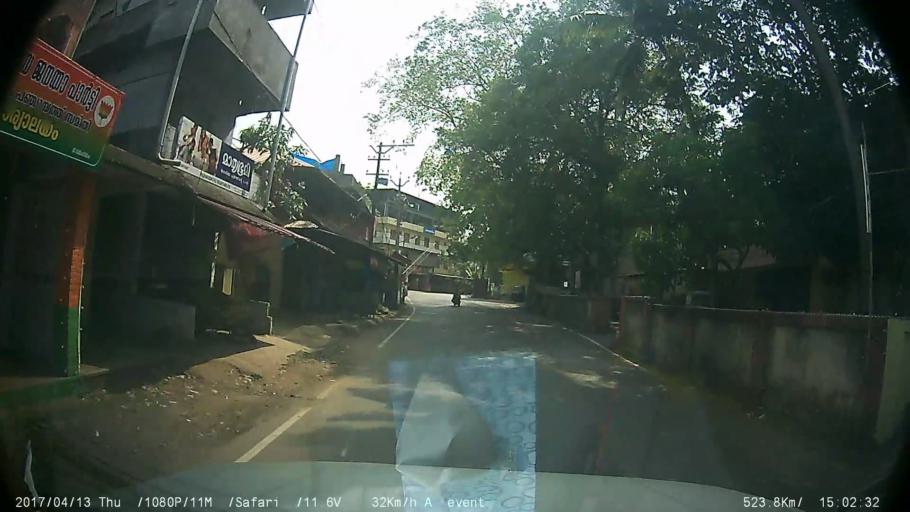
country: IN
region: Kerala
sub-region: Ernakulam
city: Ramamangalam
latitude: 9.9429
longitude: 76.4823
